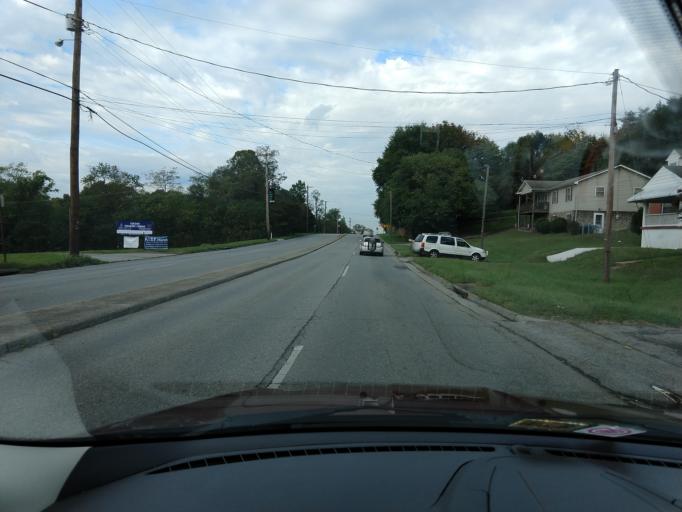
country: US
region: Virginia
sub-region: Roanoke County
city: Vinton
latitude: 37.2786
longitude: -79.8848
